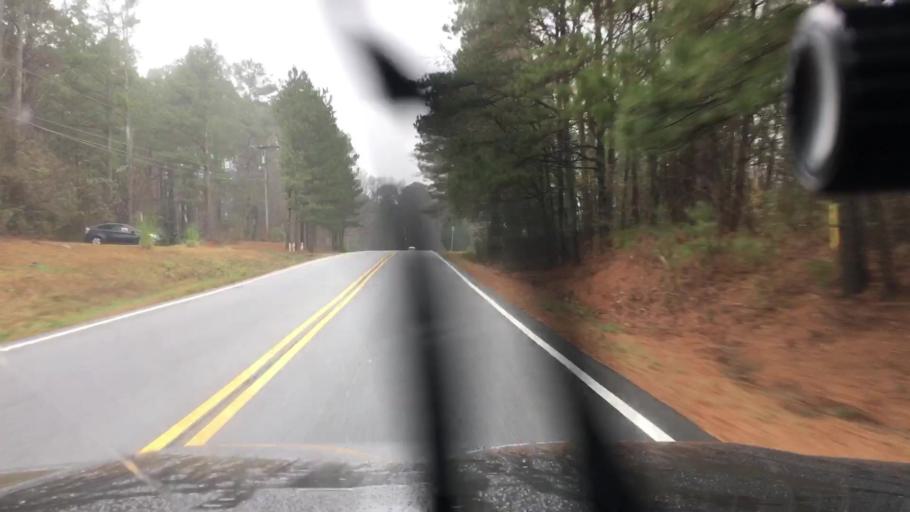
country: US
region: Georgia
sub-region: Fulton County
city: Palmetto
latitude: 33.4304
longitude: -84.6905
